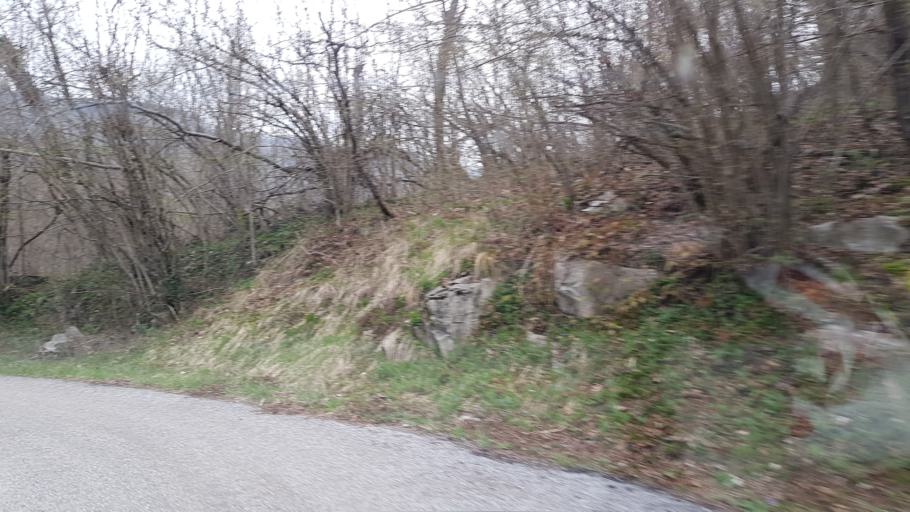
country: IT
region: Friuli Venezia Giulia
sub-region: Provincia di Udine
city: Faedis
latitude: 46.1837
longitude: 13.3963
